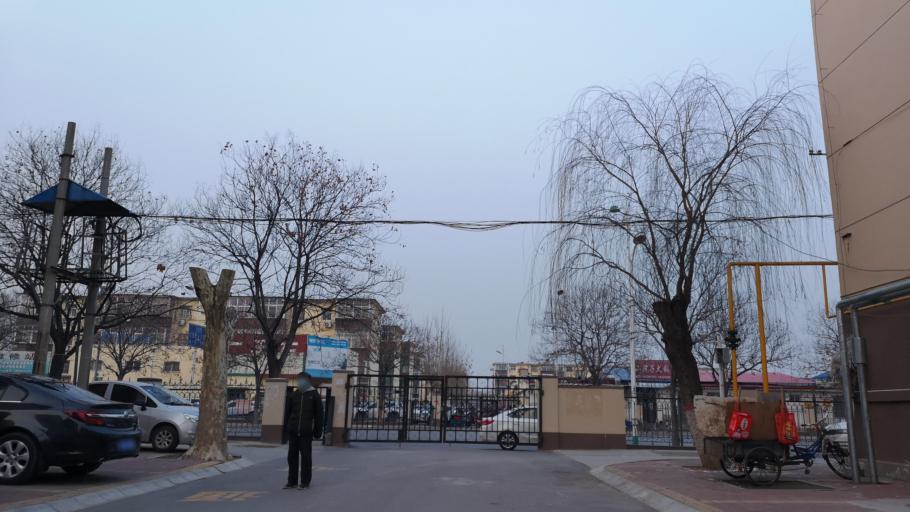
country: CN
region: Henan Sheng
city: Zhongyuanlu
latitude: 35.7844
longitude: 115.0732
